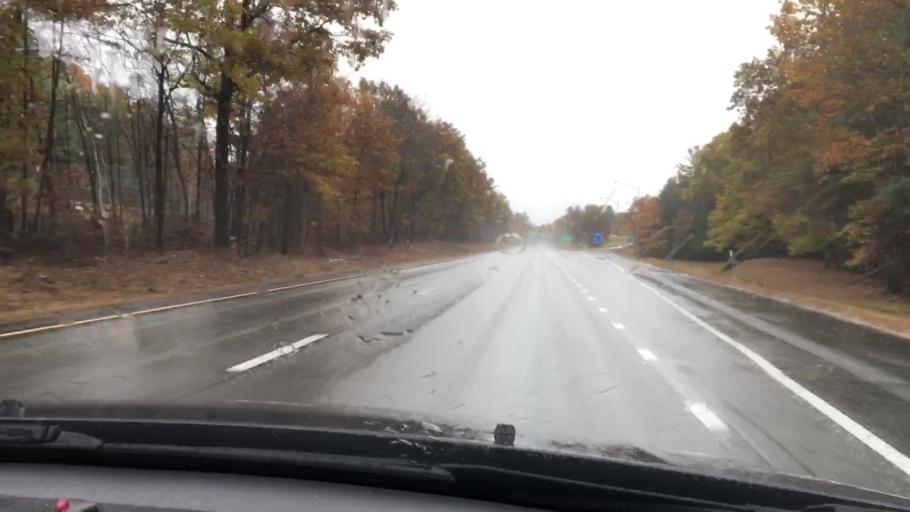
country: US
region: New Hampshire
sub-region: Merrimack County
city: Canterbury
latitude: 43.2953
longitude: -71.5767
